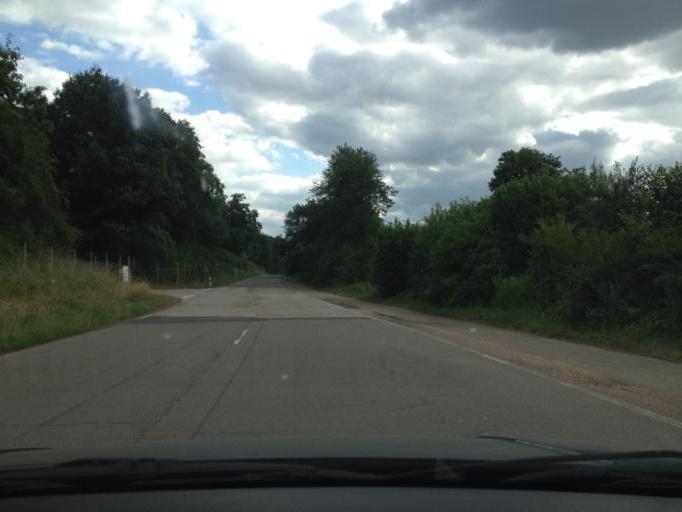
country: DE
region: Saarland
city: Sankt Wendel
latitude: 49.4568
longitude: 7.1570
